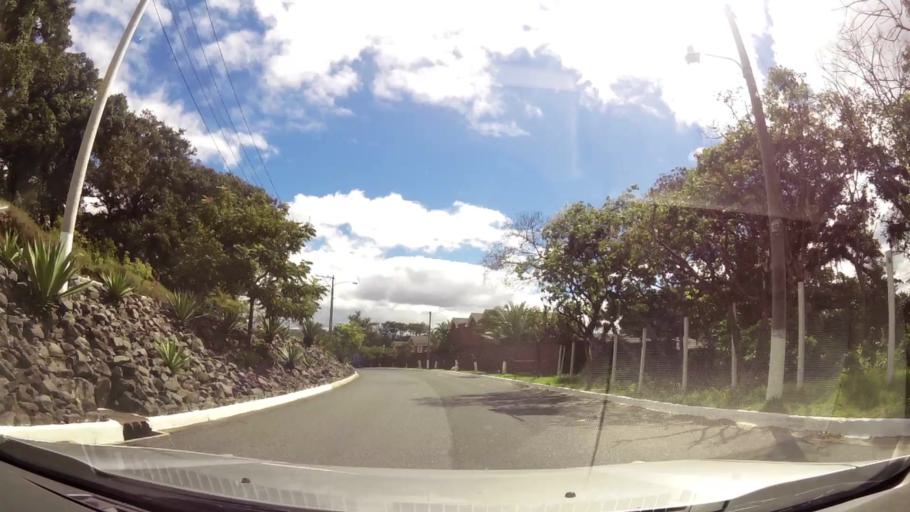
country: GT
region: Guatemala
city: Guatemala City
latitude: 14.6485
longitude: -90.5542
